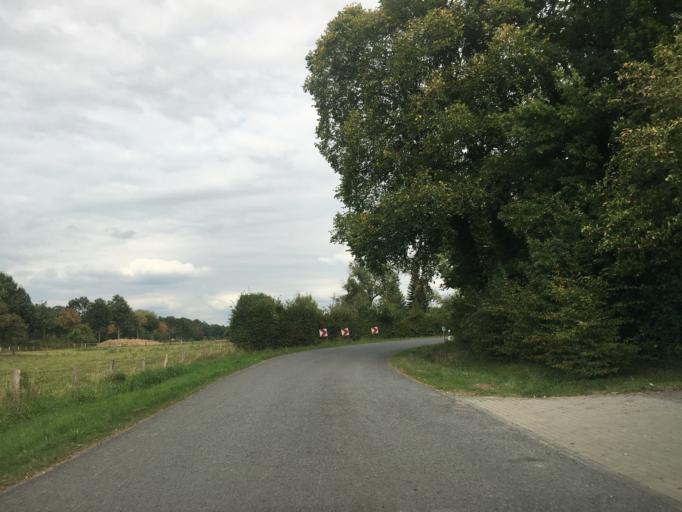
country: DE
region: North Rhine-Westphalia
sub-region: Regierungsbezirk Munster
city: Altenberge
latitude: 51.9824
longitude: 7.5322
